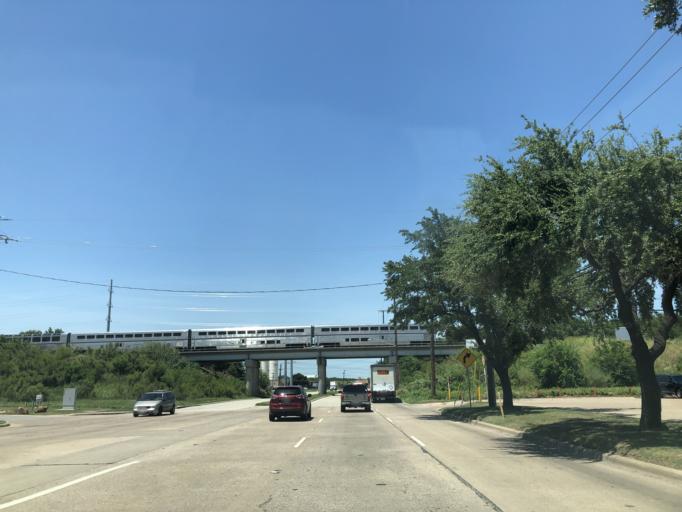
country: US
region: Texas
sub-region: Dallas County
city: Irving
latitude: 32.8129
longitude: -96.9001
